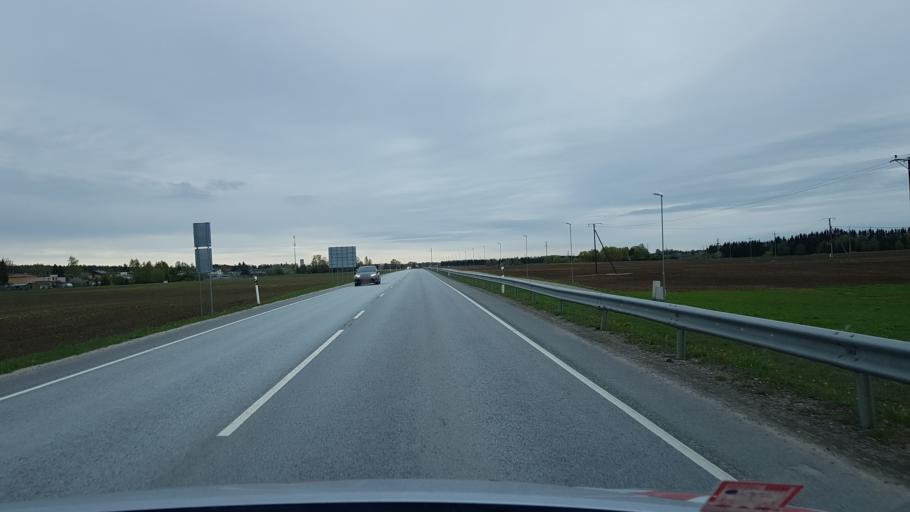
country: EE
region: Laeaene-Virumaa
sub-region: Rakvere linn
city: Rakvere
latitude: 59.3380
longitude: 26.3426
